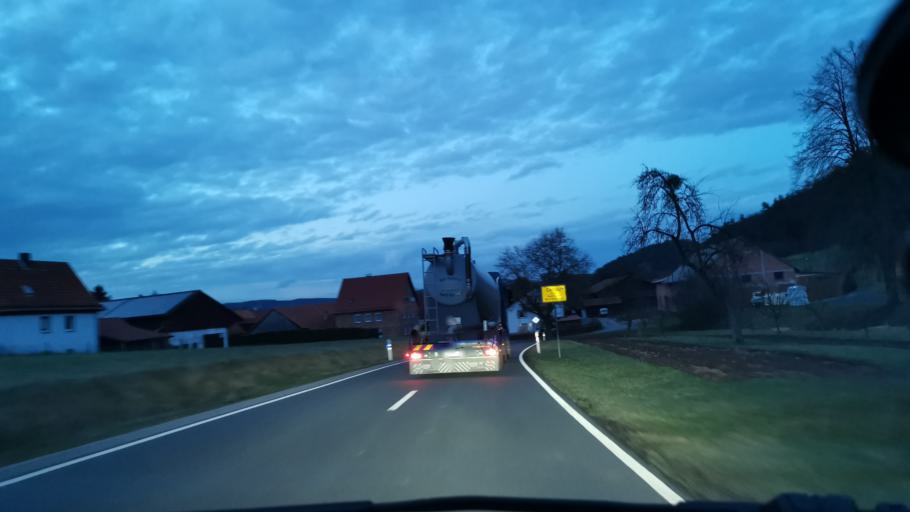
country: DE
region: Hesse
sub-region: Regierungsbezirk Kassel
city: Cornberg
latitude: 51.0951
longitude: 9.8121
